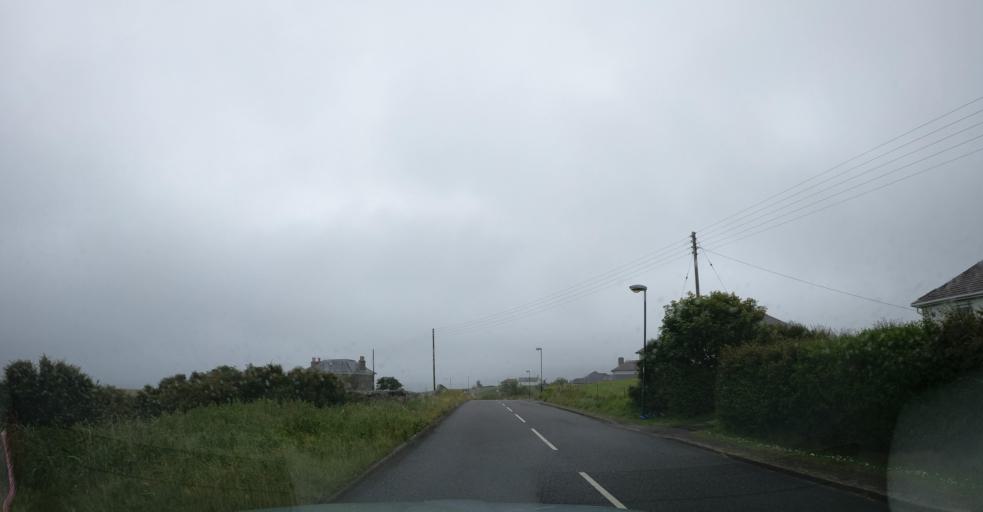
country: GB
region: Scotland
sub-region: Eilean Siar
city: Isle of North Uist
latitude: 57.6023
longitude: -7.1647
